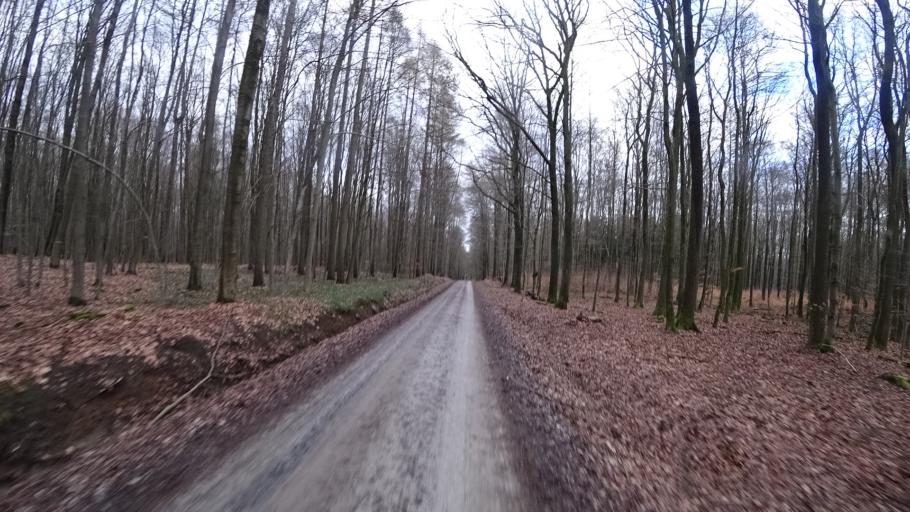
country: DE
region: Rheinland-Pfalz
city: Dernbach
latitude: 50.4235
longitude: 7.7830
